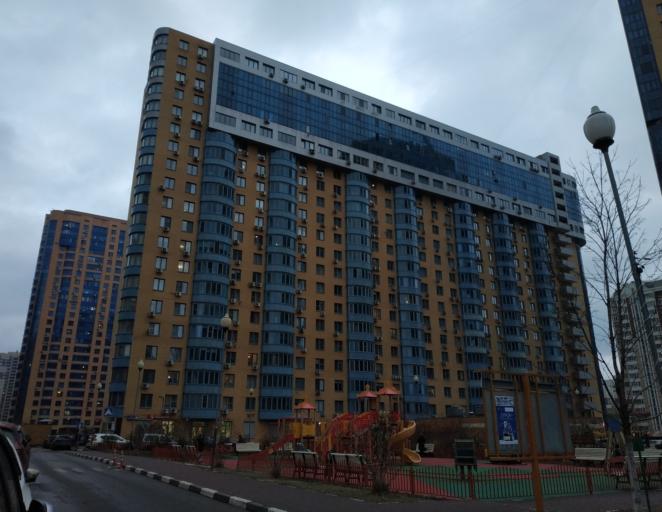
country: RU
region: Moskovskaya
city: Reutov
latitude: 55.7537
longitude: 37.8776
